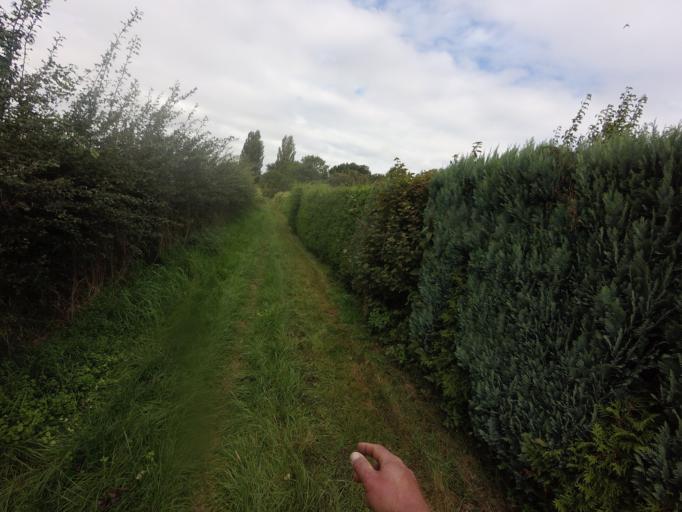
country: NL
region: Limburg
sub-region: Eijsden-Margraten
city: Margraten
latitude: 50.8148
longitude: 5.8261
